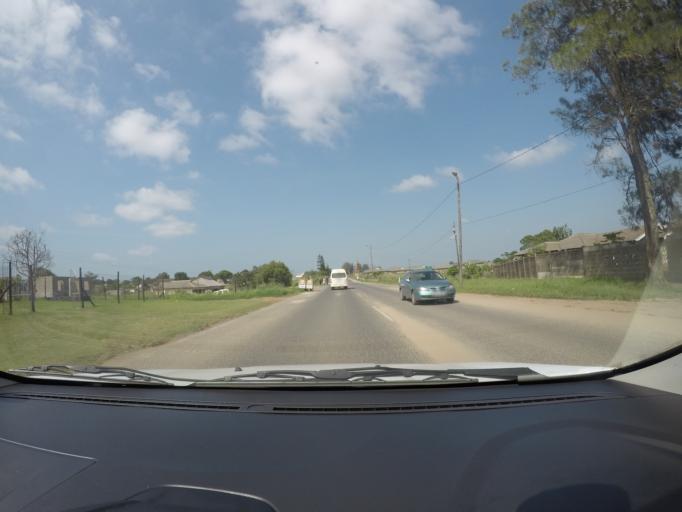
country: ZA
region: KwaZulu-Natal
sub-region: uThungulu District Municipality
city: eSikhawini
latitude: -28.8870
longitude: 31.8979
